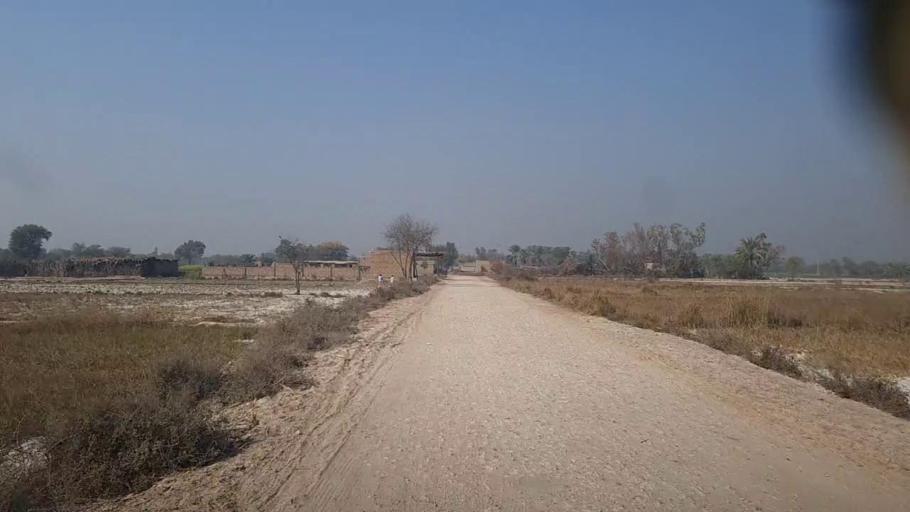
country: PK
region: Sindh
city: Karaundi
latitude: 26.8474
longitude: 68.3898
